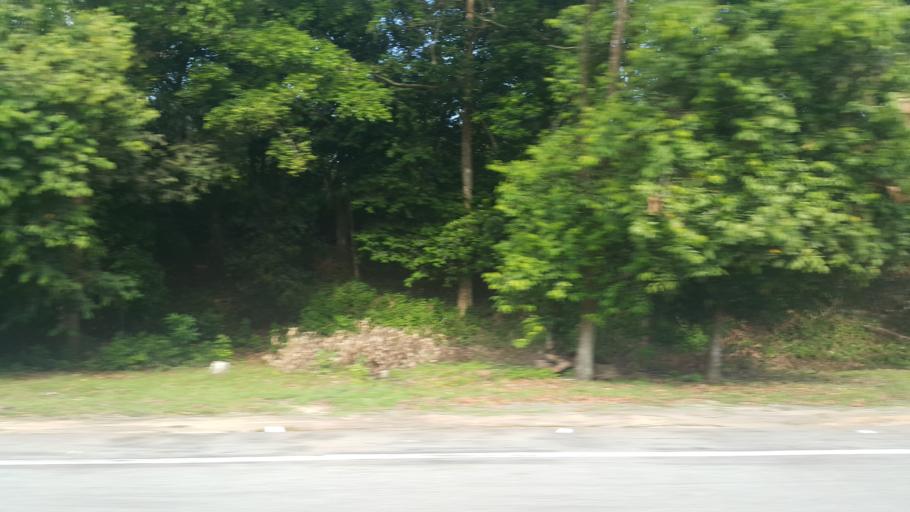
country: MY
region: Johor
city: Taman Senai
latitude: 1.6030
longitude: 103.6146
